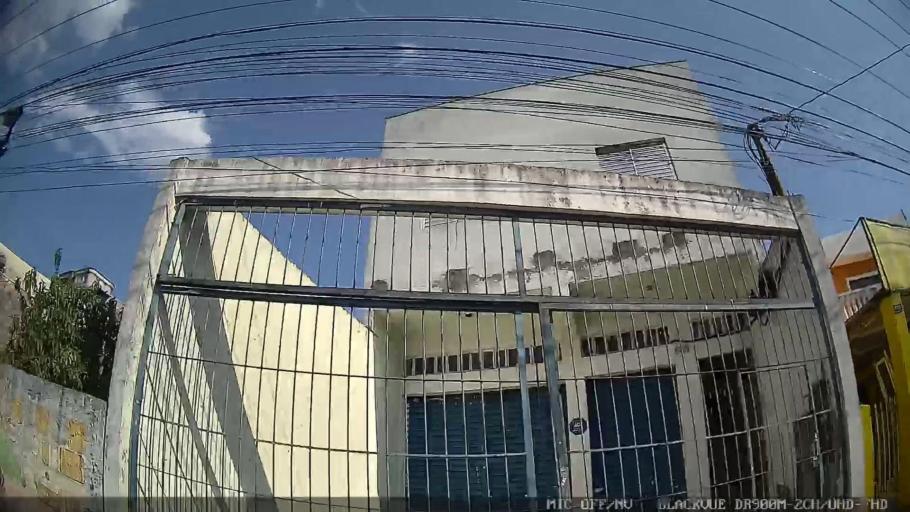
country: BR
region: Sao Paulo
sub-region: Ferraz De Vasconcelos
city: Ferraz de Vasconcelos
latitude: -23.5164
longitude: -46.4373
